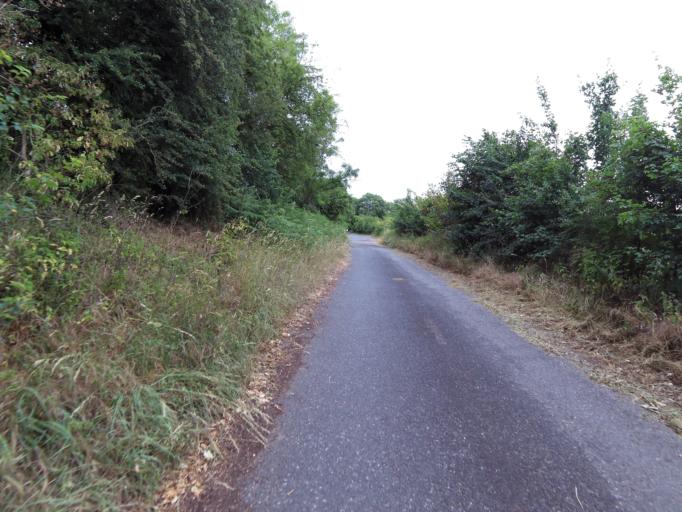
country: GB
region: England
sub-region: Suffolk
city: Bungay
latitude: 52.4355
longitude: 1.3837
